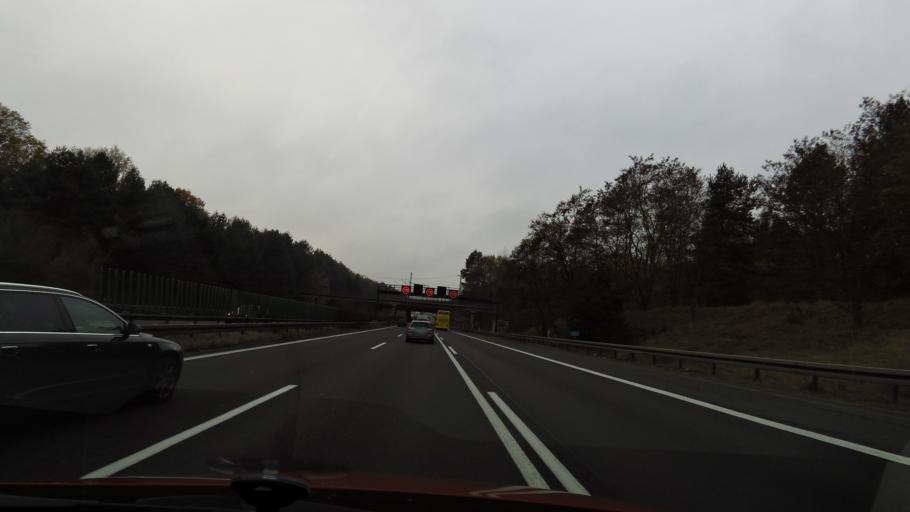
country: DE
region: Brandenburg
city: Michendorf
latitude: 52.3035
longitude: 13.0107
